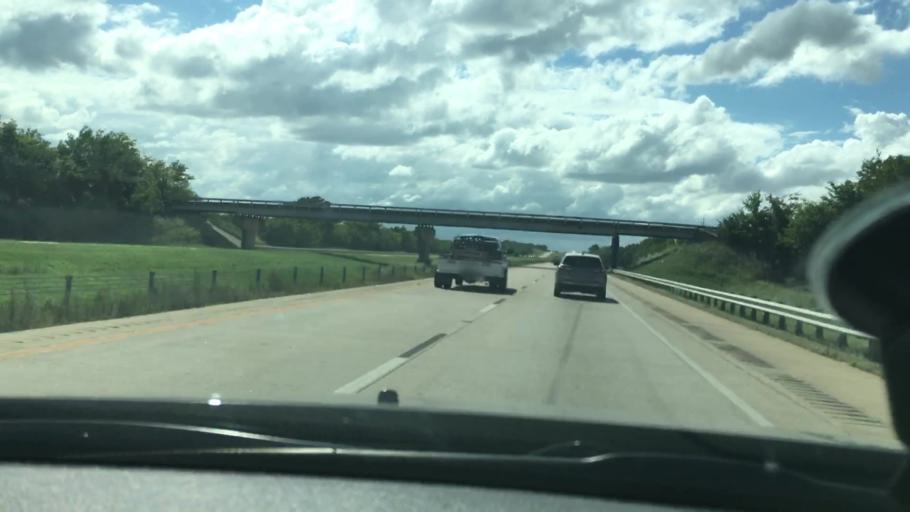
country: US
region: Oklahoma
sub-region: McIntosh County
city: Checotah
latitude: 35.4579
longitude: -95.5562
